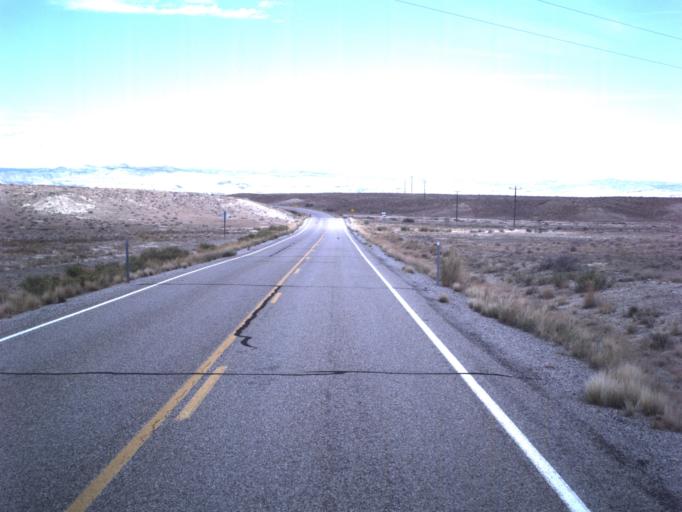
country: US
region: Utah
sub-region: Grand County
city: Moab
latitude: 38.9377
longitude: -109.3477
